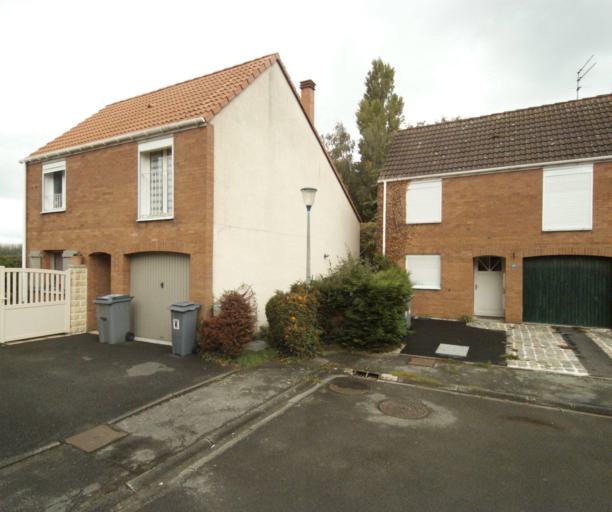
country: FR
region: Nord-Pas-de-Calais
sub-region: Departement du Nord
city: Wavrin
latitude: 50.5739
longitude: 2.9471
